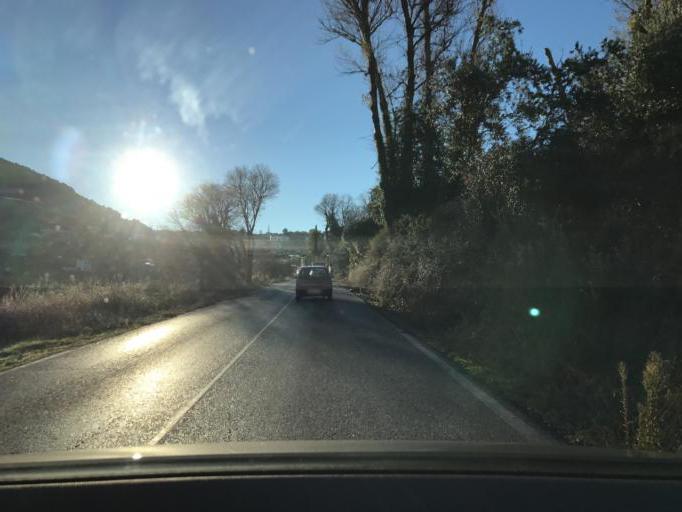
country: ES
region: Andalusia
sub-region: Provincia de Granada
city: Nivar
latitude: 37.2658
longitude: -3.5808
